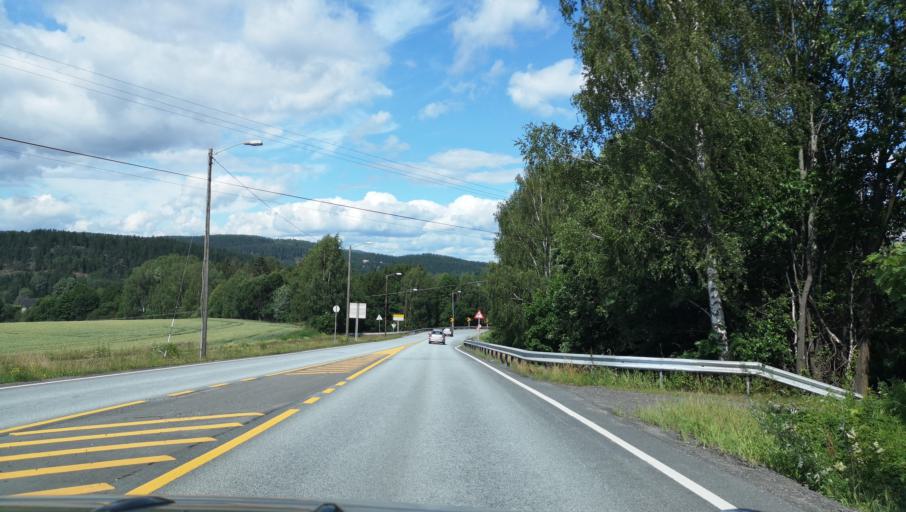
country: NO
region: Buskerud
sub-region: Modum
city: Vikersund
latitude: 59.8888
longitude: 9.9224
